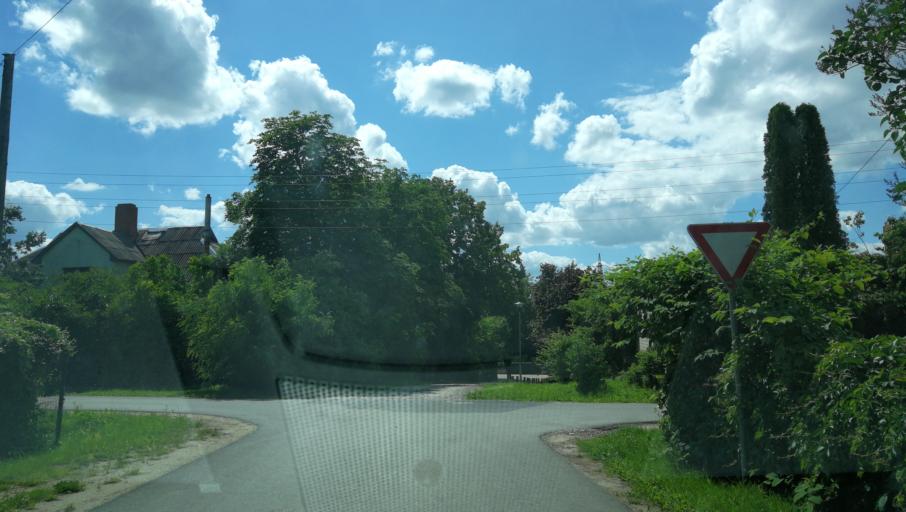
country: LV
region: Broceni
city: Broceni
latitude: 56.6744
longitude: 22.5674
